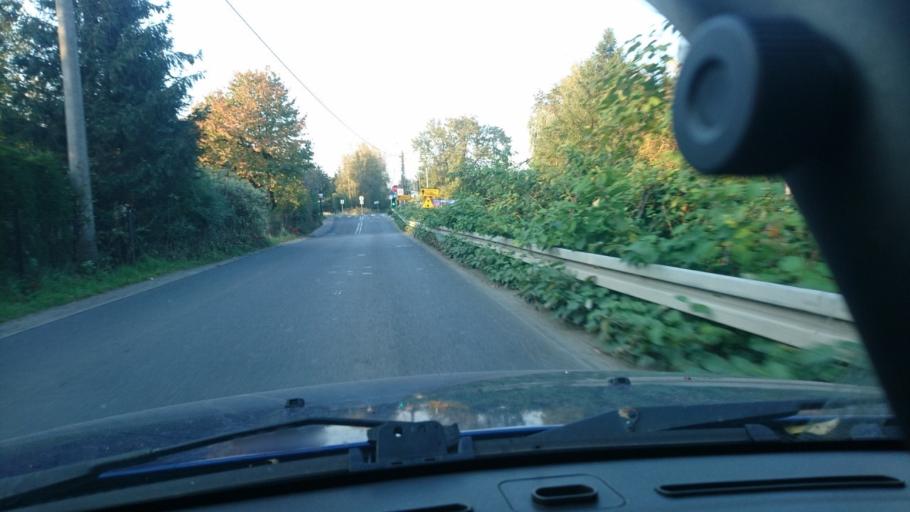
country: PL
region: Silesian Voivodeship
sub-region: Powiat bielski
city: Mazancowice
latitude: 49.8205
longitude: 18.9804
